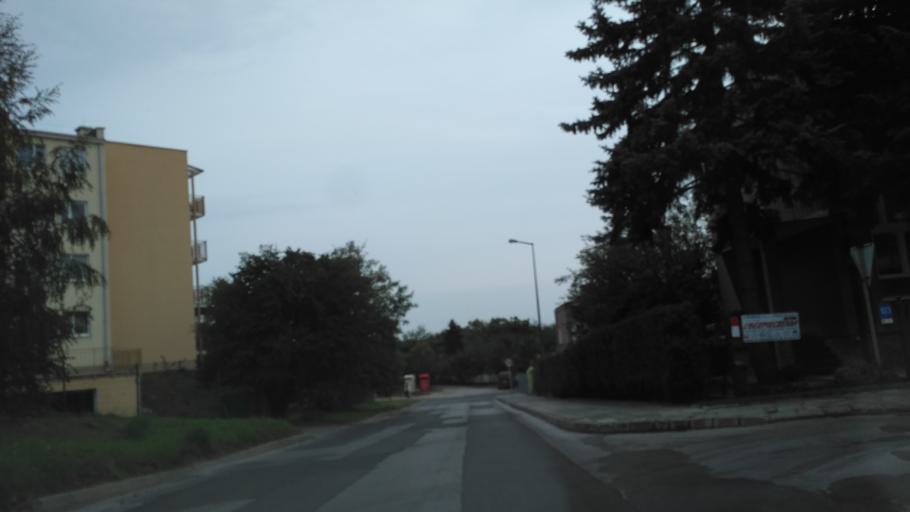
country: PL
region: Lublin Voivodeship
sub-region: Powiat lubelski
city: Lublin
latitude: 51.2263
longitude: 22.5937
